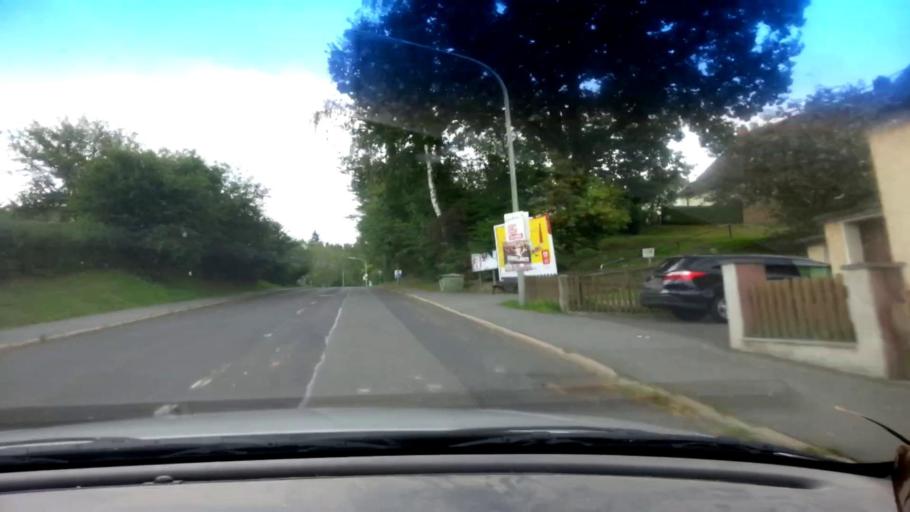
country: DE
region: Bavaria
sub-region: Upper Franconia
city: Schirnding
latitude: 50.0762
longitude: 12.2327
